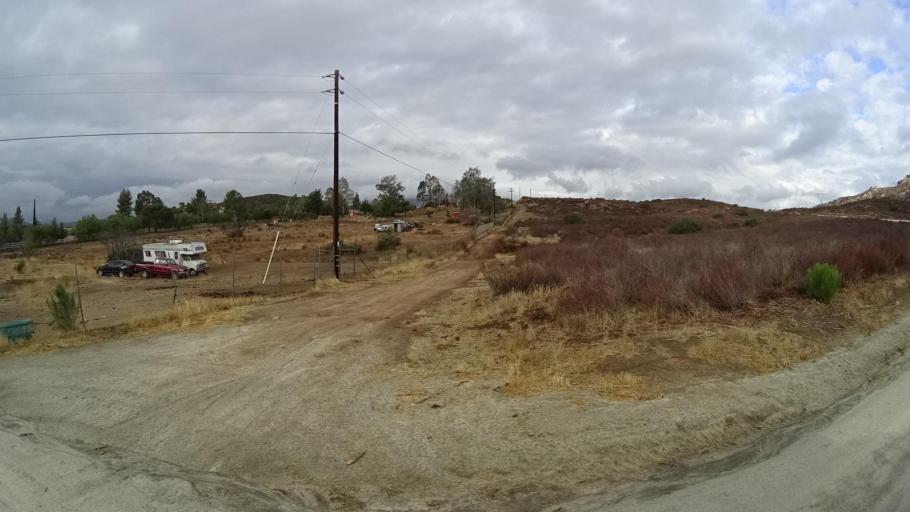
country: MX
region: Baja California
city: Tecate
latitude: 32.5896
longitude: -116.6231
